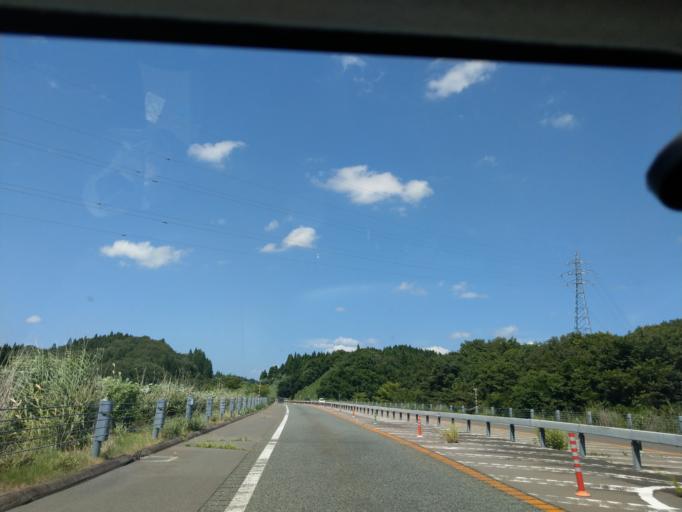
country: JP
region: Akita
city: Akita
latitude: 39.6690
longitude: 140.1883
